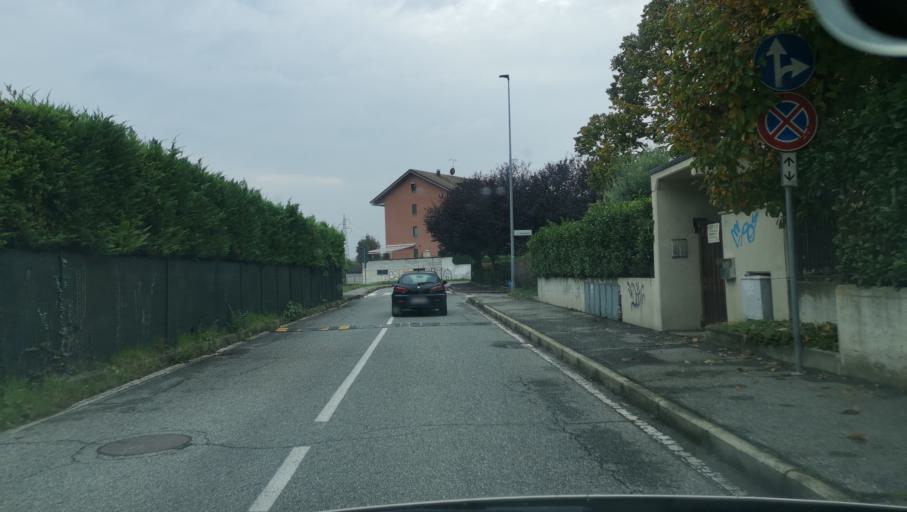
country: IT
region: Piedmont
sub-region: Provincia di Torino
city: Settimo Torinese
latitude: 45.1316
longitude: 7.7743
